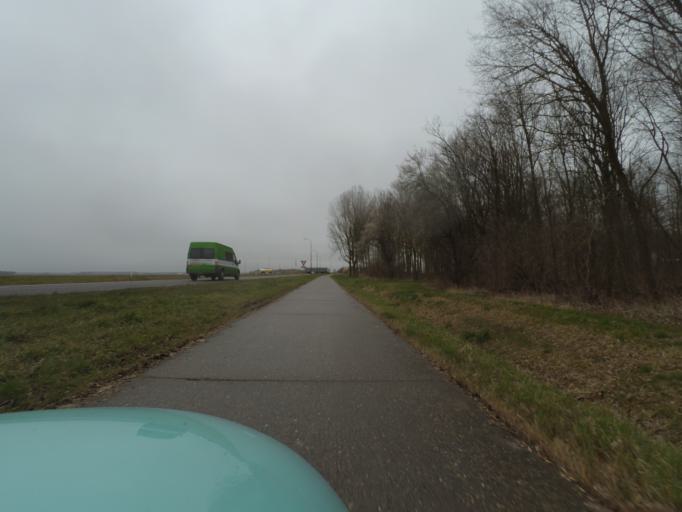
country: NL
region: Flevoland
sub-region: Gemeente Dronten
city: Dronten
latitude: 52.5378
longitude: 5.7360
